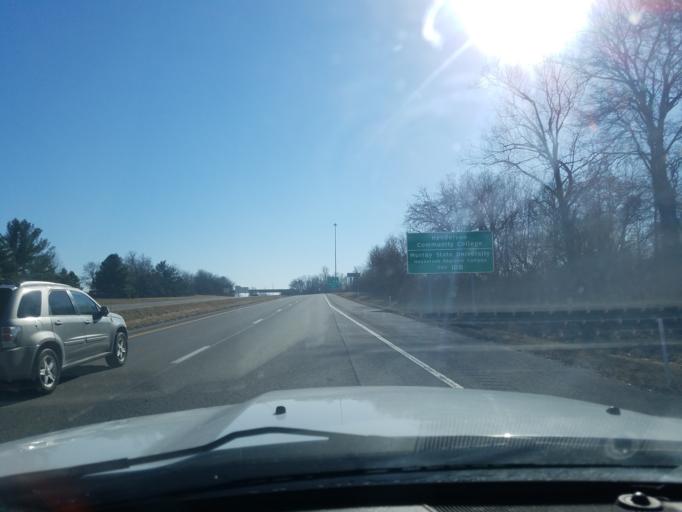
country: US
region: Kentucky
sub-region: Henderson County
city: Henderson
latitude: 37.8094
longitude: -87.5641
